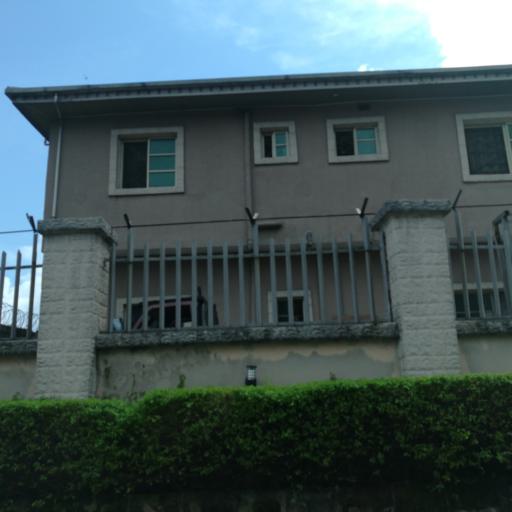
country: NG
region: Rivers
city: Port Harcourt
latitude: 4.8103
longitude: 7.0655
